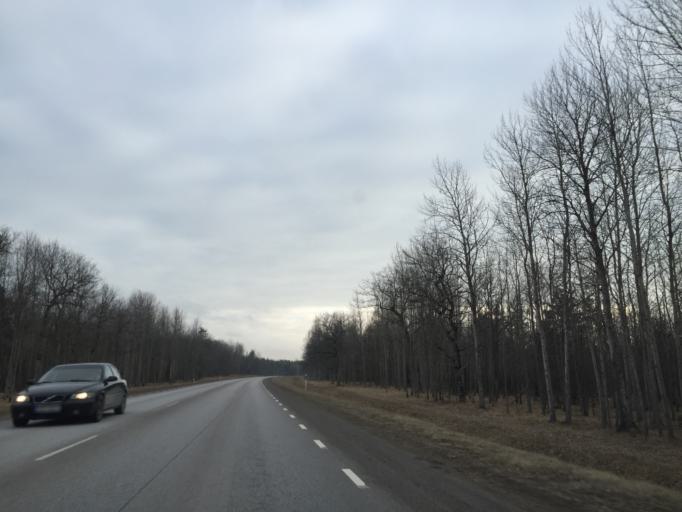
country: EE
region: Saare
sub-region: Orissaare vald
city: Orissaare
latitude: 58.4657
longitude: 22.8142
